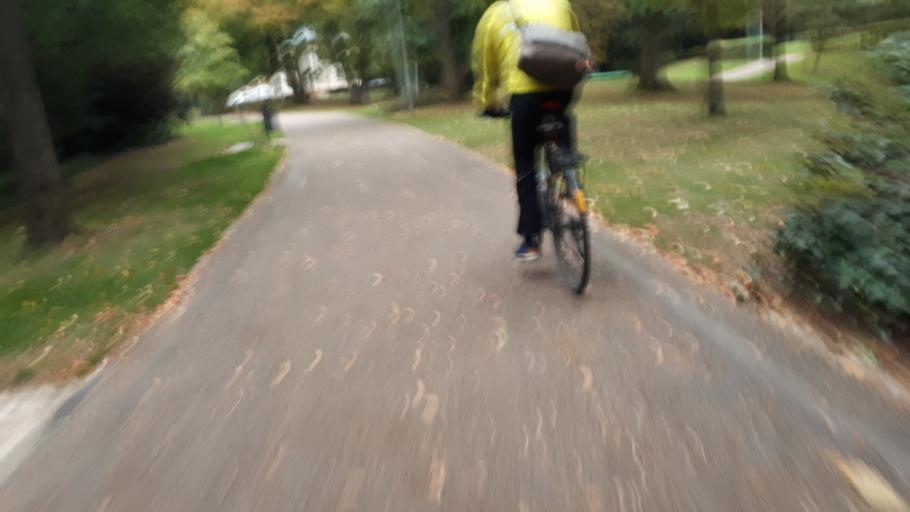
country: LU
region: Luxembourg
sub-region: Canton de Luxembourg
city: Luxembourg
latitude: 49.6134
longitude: 6.1221
